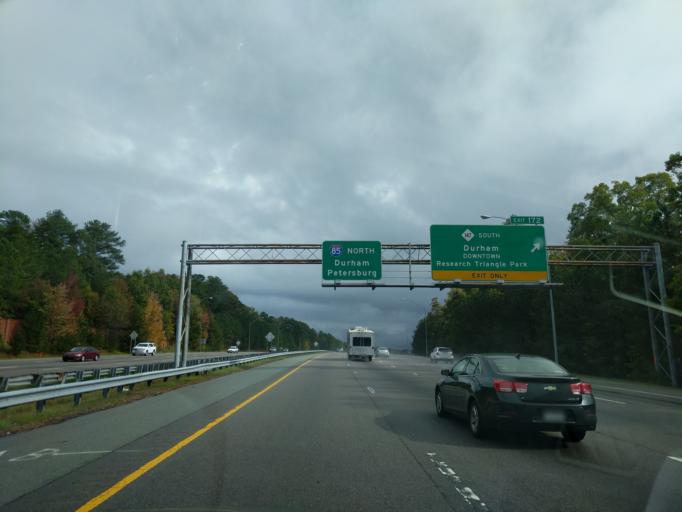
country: US
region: North Carolina
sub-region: Durham County
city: Durham
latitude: 36.0366
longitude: -78.9736
